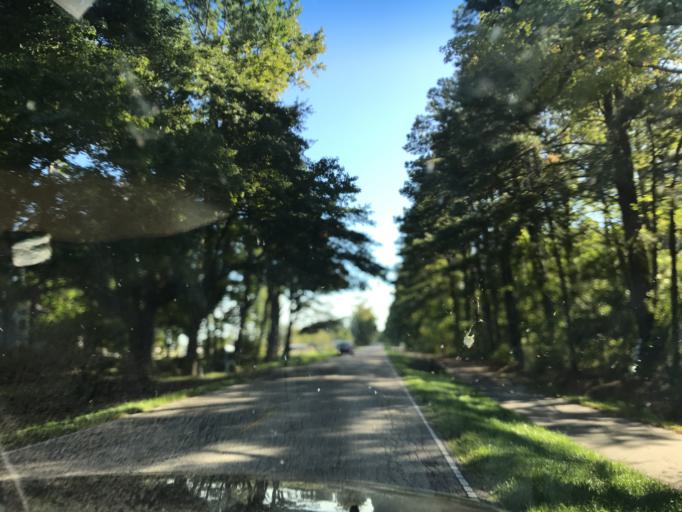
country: US
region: Virginia
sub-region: City of Portsmouth
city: Portsmouth Heights
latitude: 36.7153
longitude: -76.3520
